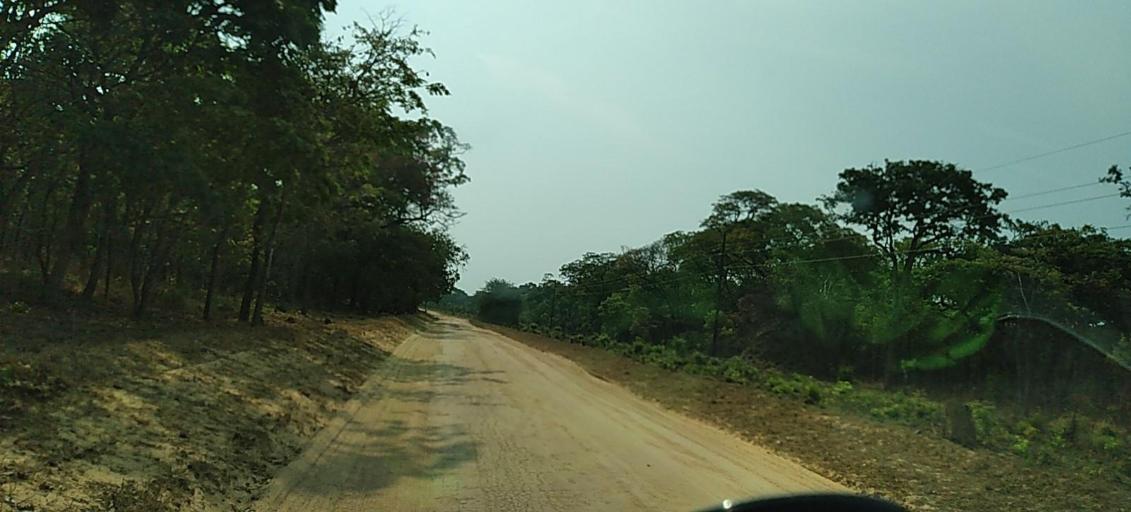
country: ZM
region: North-Western
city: Solwezi
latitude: -12.6837
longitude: 26.3896
